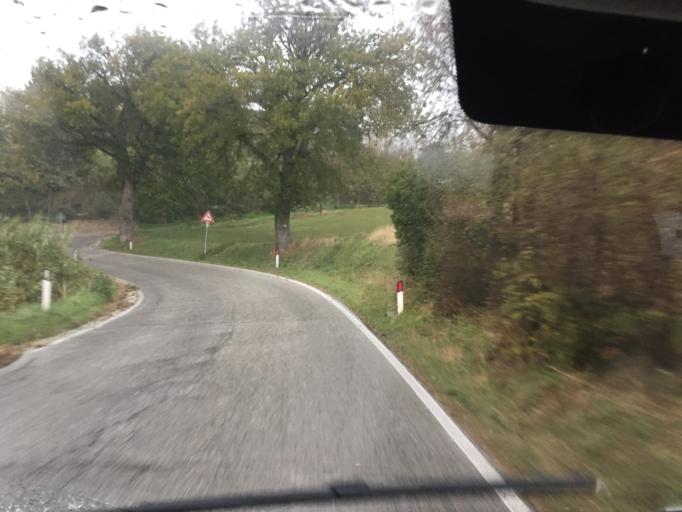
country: IT
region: The Marches
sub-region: Provincia di Macerata
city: Camerino
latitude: 43.1243
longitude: 13.0651
